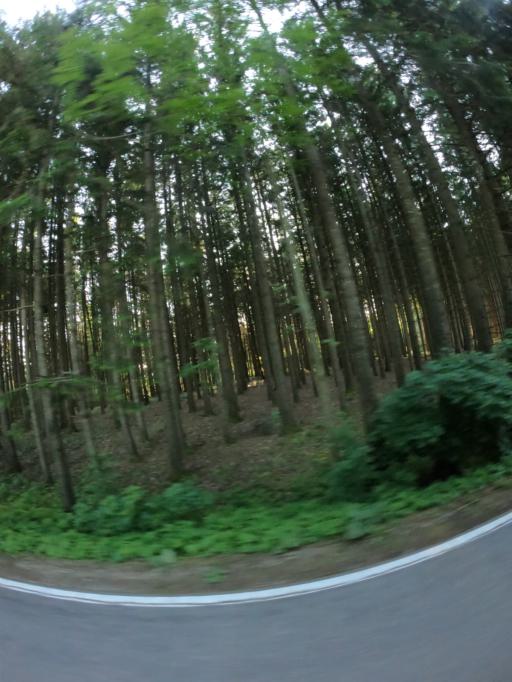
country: DE
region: Bavaria
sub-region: Upper Bavaria
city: Inning am Holz
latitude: 48.3429
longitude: 12.0708
